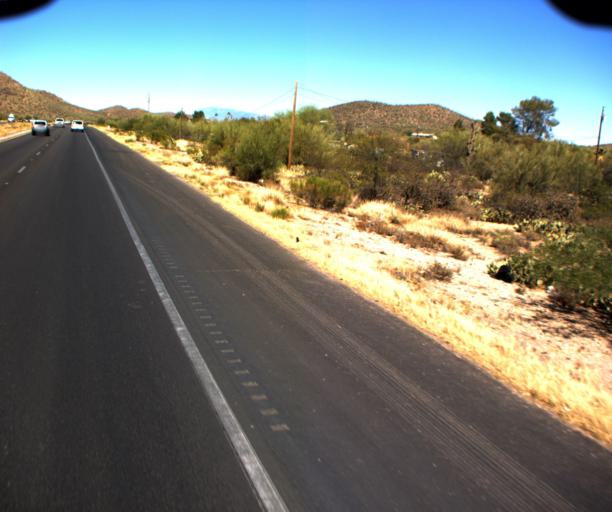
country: US
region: Arizona
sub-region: Pima County
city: Tucson Estates
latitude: 32.1760
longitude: -111.0541
